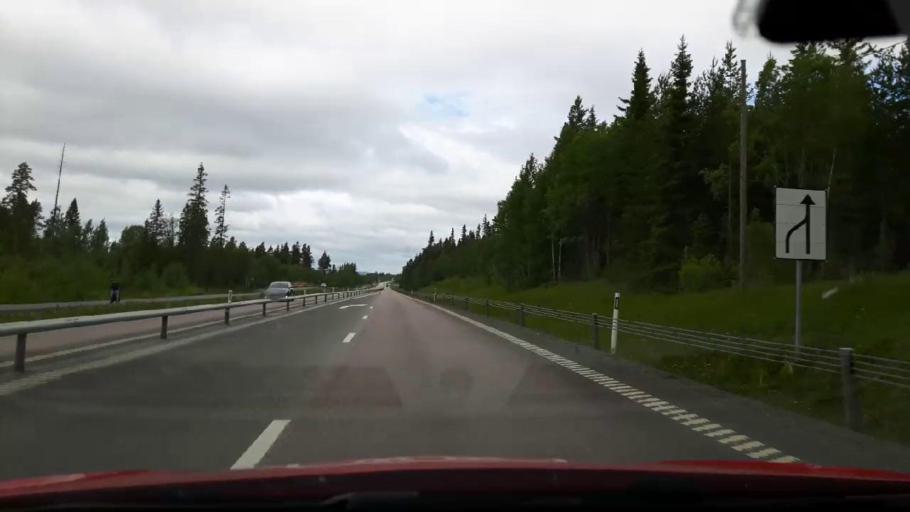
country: SE
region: Jaemtland
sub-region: Krokoms Kommun
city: Krokom
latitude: 63.2773
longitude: 14.5287
